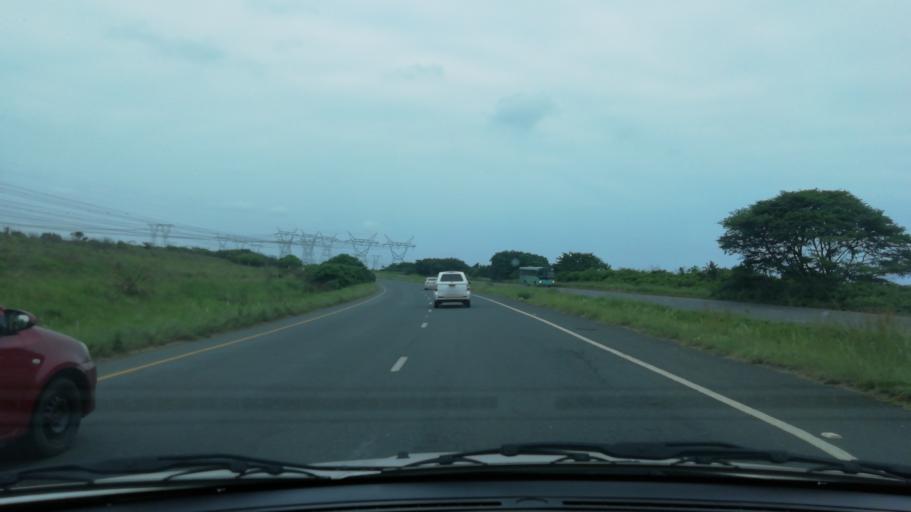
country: ZA
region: KwaZulu-Natal
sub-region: uThungulu District Municipality
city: Richards Bay
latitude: -28.7800
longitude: 31.9992
